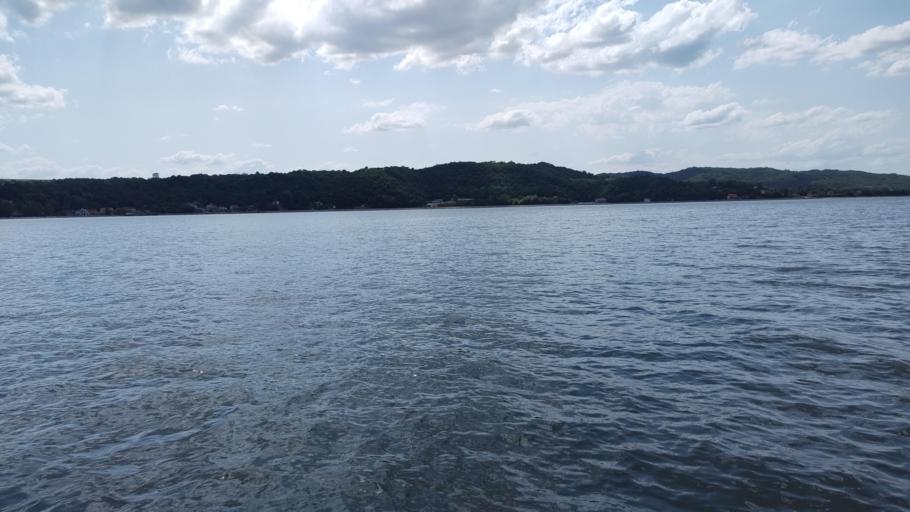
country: RS
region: Central Serbia
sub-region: Branicevski Okrug
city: Golubac
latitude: 44.6606
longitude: 21.6320
